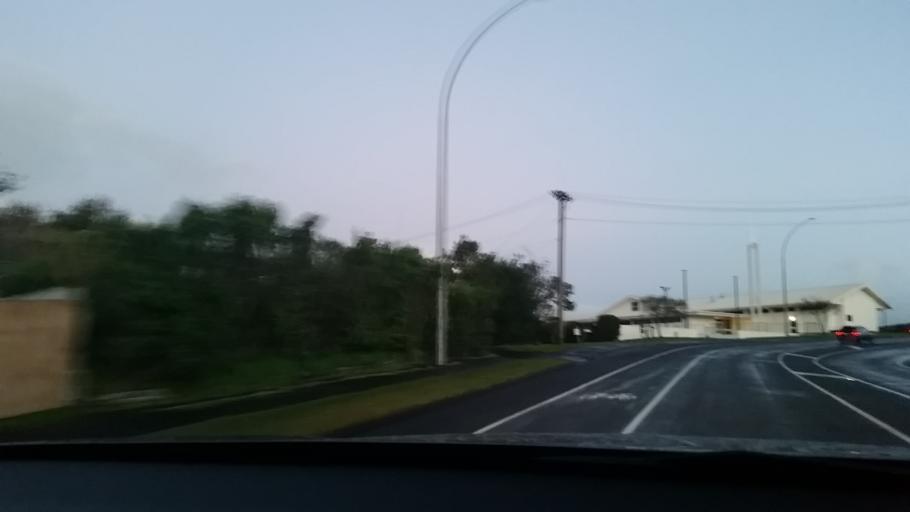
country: NZ
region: Waikato
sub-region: Hamilton City
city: Hamilton
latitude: -37.7986
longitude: 175.2480
